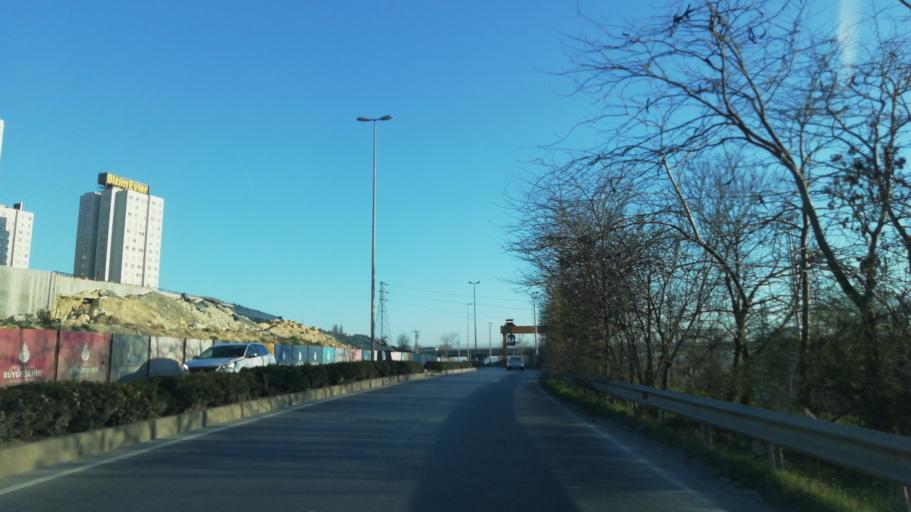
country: TR
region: Istanbul
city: Esenyurt
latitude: 41.0625
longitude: 28.7001
